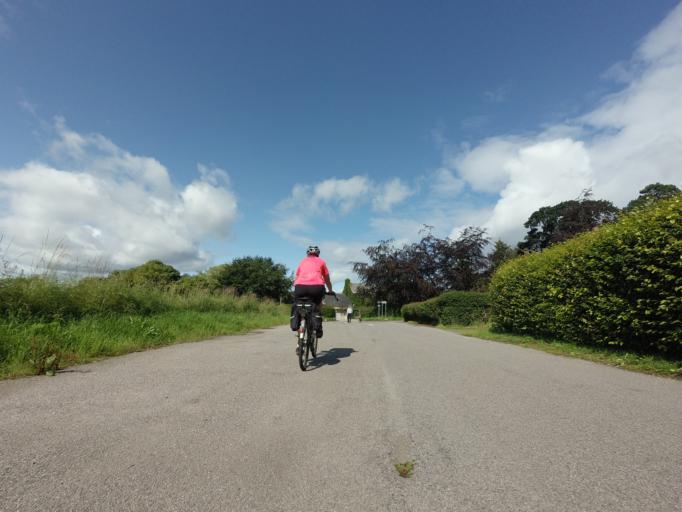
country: GB
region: Scotland
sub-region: Moray
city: Kinloss
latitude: 57.6451
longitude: -3.5206
